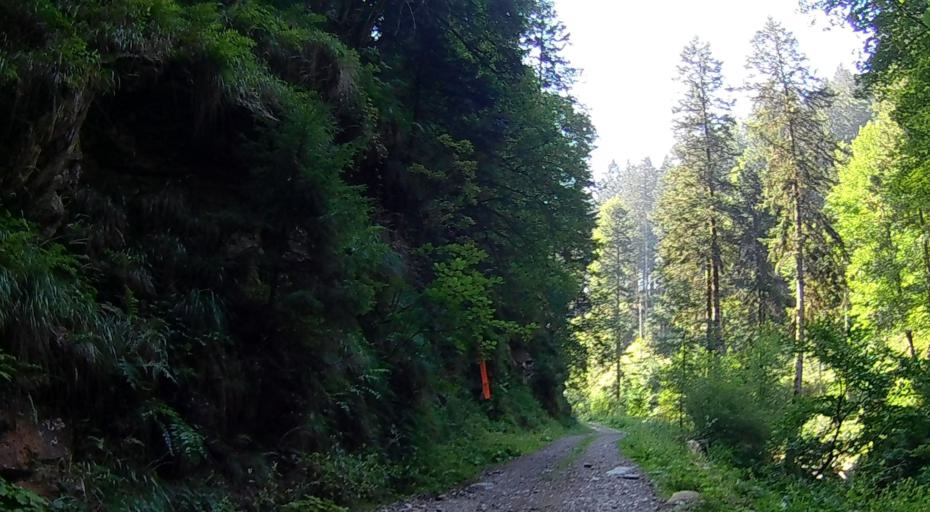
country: SI
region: Selnica ob Dravi
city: Selnica ob Dravi
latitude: 46.5047
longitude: 15.4549
